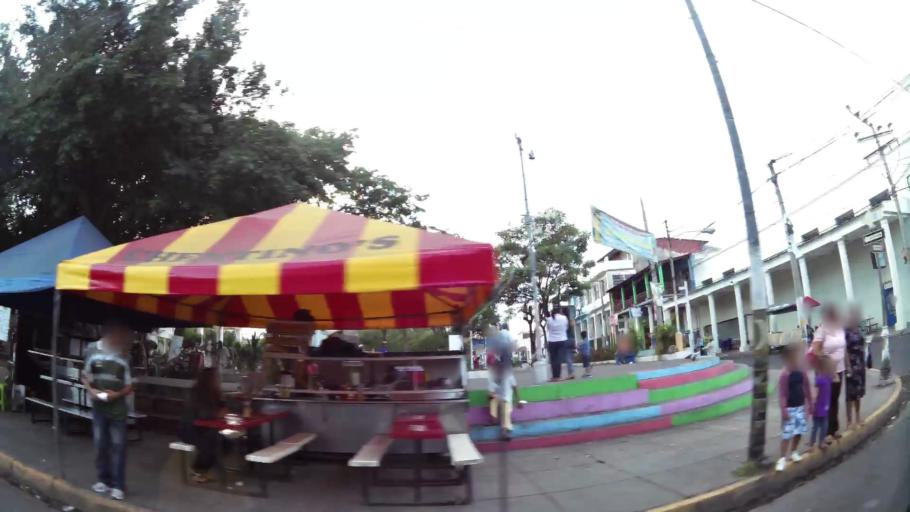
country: SV
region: San Vicente
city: San Vicente
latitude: 13.6455
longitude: -88.7837
